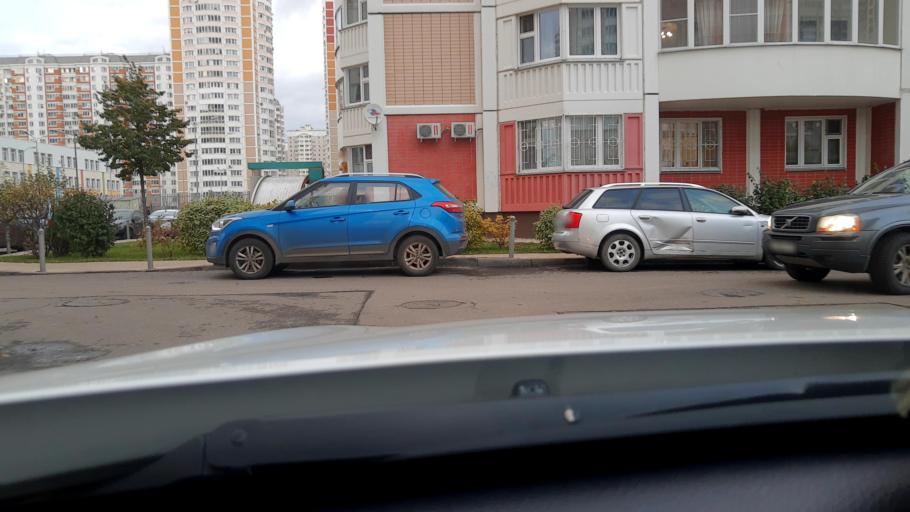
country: RU
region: Moskovskaya
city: Moskovskiy
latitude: 55.5996
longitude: 37.3611
